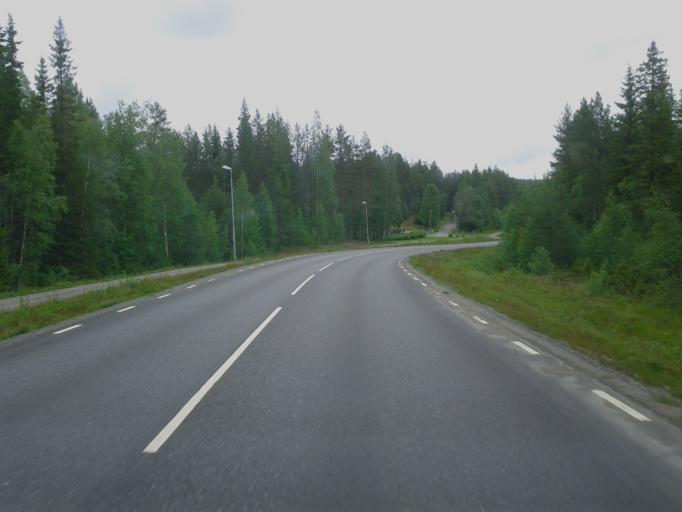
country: SE
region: Vaesterbotten
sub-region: Skelleftea Kommun
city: Boliden
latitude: 64.8750
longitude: 20.3878
